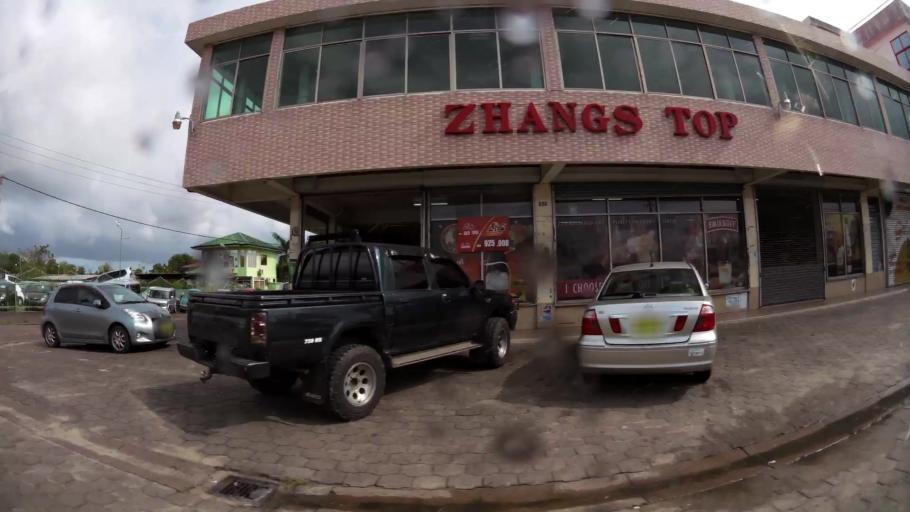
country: SR
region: Paramaribo
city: Paramaribo
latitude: 5.8420
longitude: -55.1990
